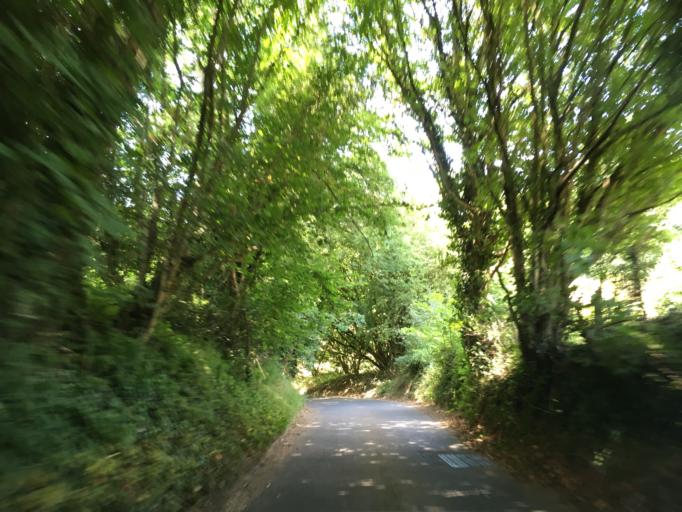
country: GB
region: England
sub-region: Gloucestershire
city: Painswick
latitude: 51.7866
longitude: -2.2059
